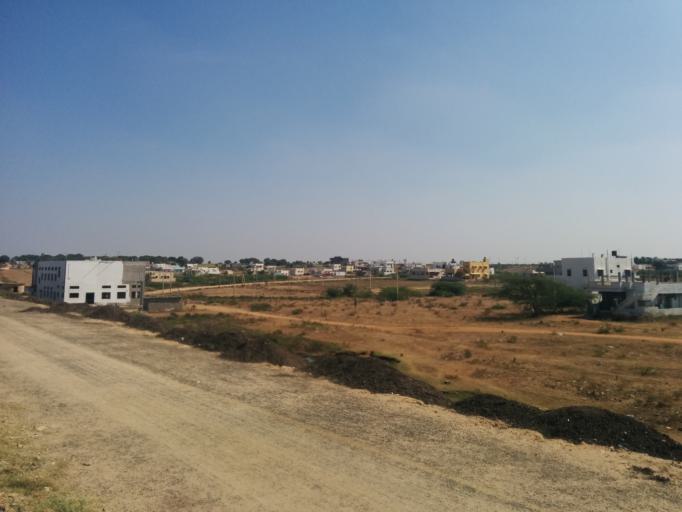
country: IN
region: Karnataka
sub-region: Gadag
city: Gadag
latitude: 15.4378
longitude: 75.6557
